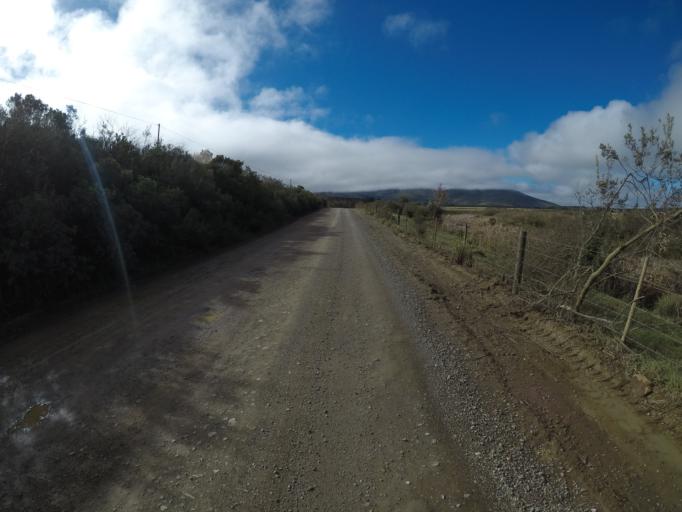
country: ZA
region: Western Cape
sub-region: Cape Winelands District Municipality
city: Ashton
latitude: -34.1229
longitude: 19.8325
